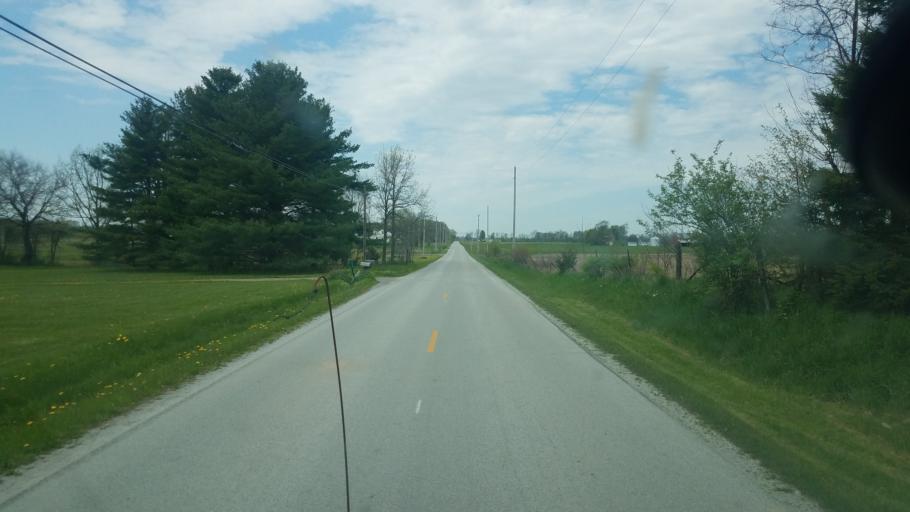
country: US
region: Ohio
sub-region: Hardin County
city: Ada
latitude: 40.7620
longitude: -83.8542
